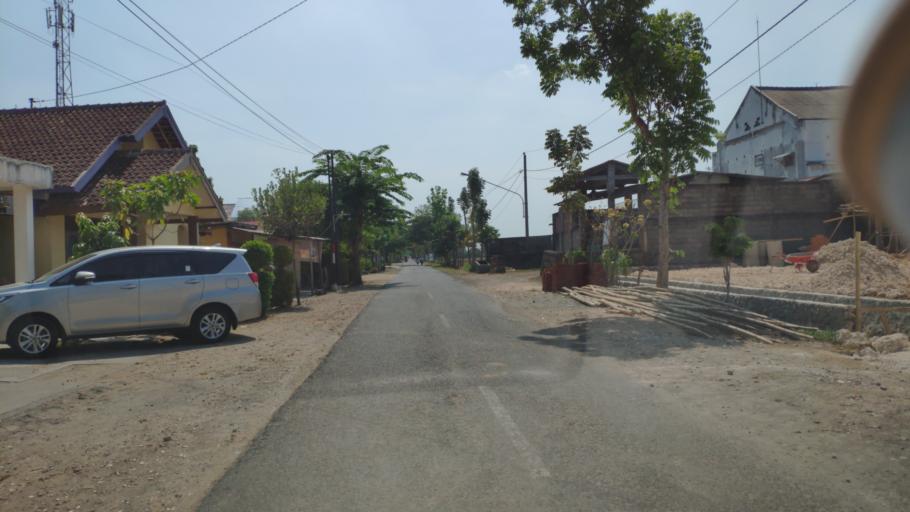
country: ID
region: Central Java
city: Kedungjenar
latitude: -6.9794
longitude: 111.4196
